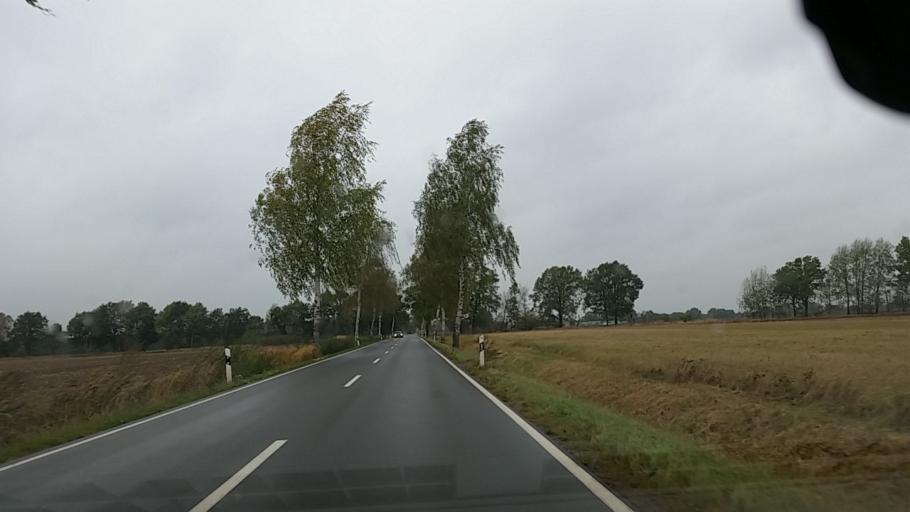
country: DE
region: Lower Saxony
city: Tiddische
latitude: 52.4888
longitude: 10.8089
